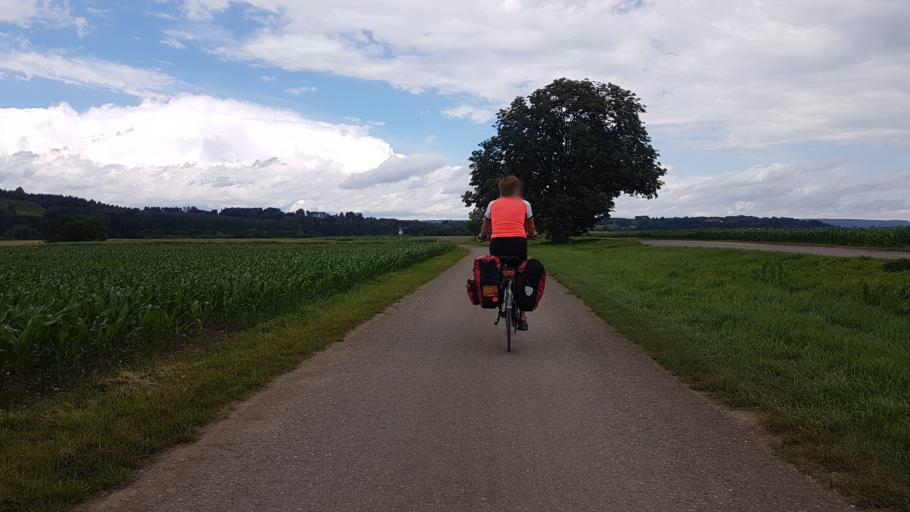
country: DE
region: Baden-Wuerttemberg
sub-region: Tuebingen Region
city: Herbertingen
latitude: 48.0899
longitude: 9.4234
